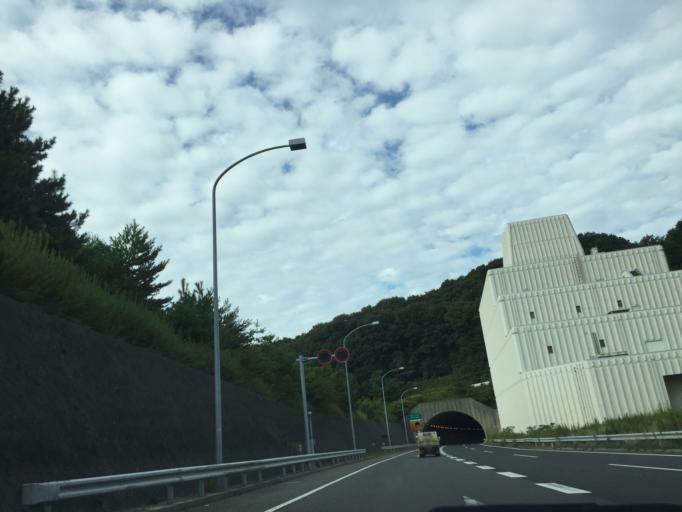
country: JP
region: Hyogo
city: Akashi
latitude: 34.6543
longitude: 135.0643
